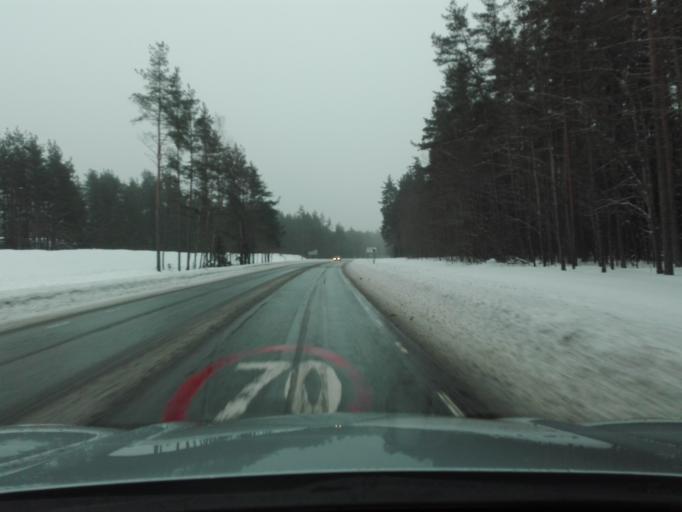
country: EE
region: Harju
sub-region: Kiili vald
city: Kiili
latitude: 59.3522
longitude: 24.7737
